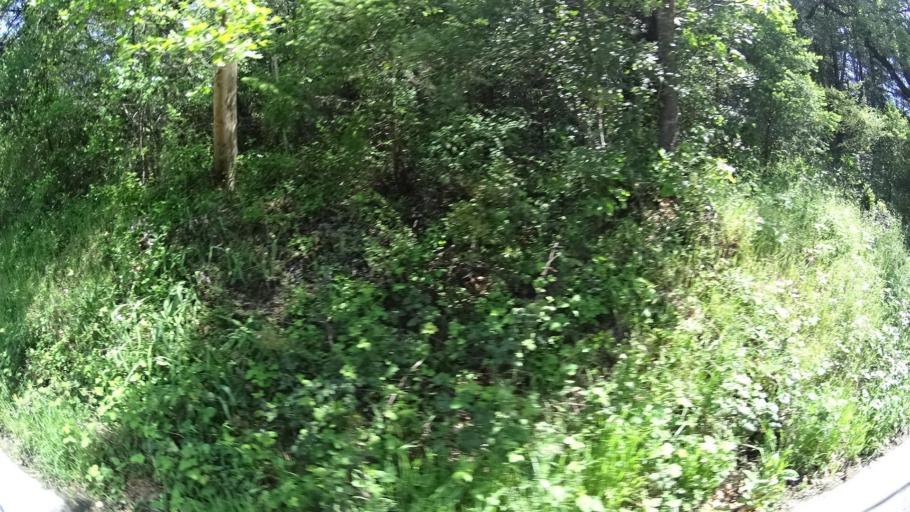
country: US
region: California
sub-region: Humboldt County
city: Redway
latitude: 40.1745
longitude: -123.6108
